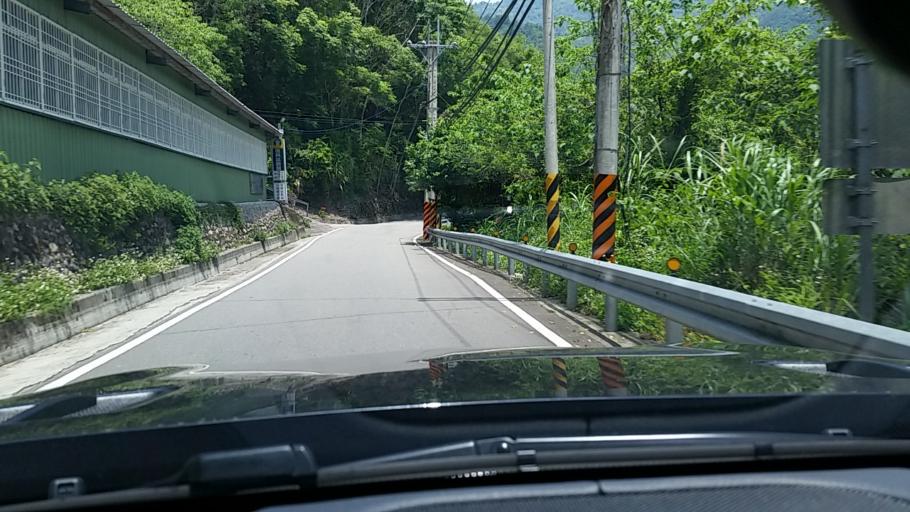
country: TW
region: Taiwan
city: Daxi
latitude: 24.6948
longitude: 121.3743
